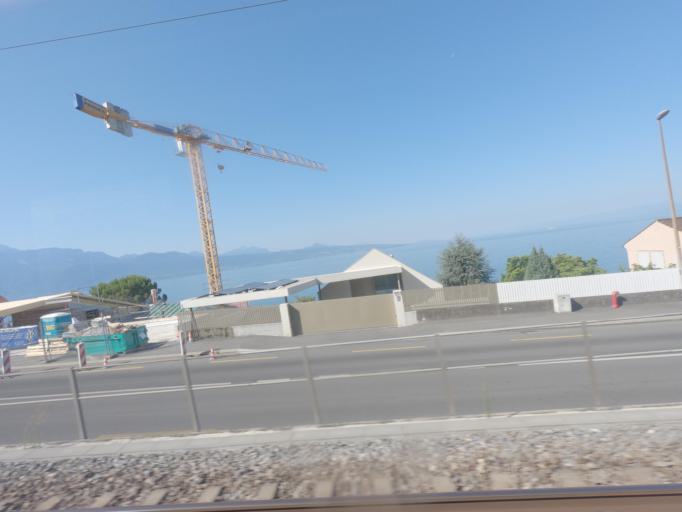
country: CH
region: Vaud
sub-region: Lavaux-Oron District
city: Cully
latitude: 46.4930
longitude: 6.7112
